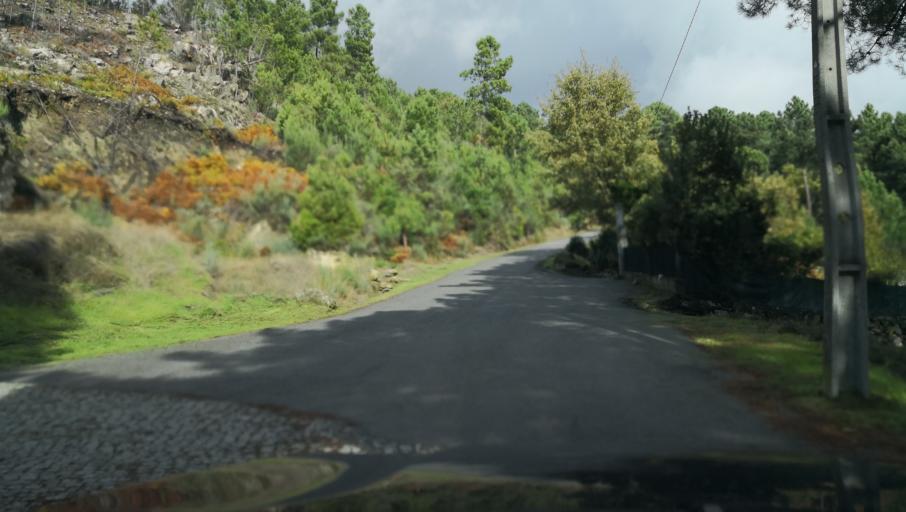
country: PT
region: Vila Real
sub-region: Vila Real
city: Vila Real
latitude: 41.3237
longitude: -7.7588
